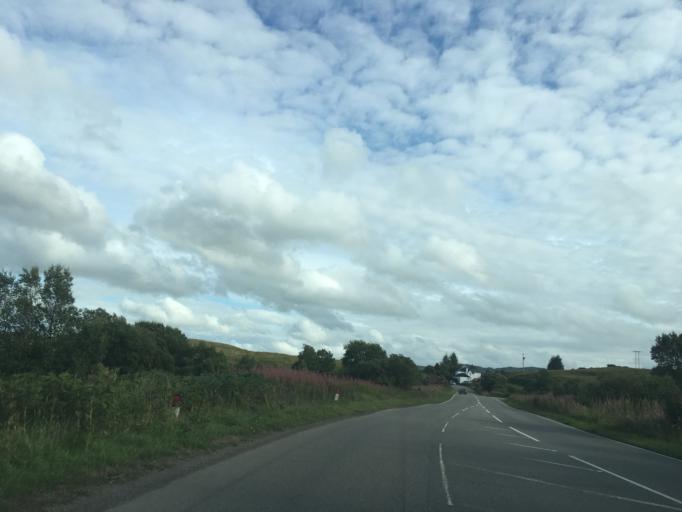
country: GB
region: Scotland
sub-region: Argyll and Bute
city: Oban
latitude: 56.3922
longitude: -5.4614
